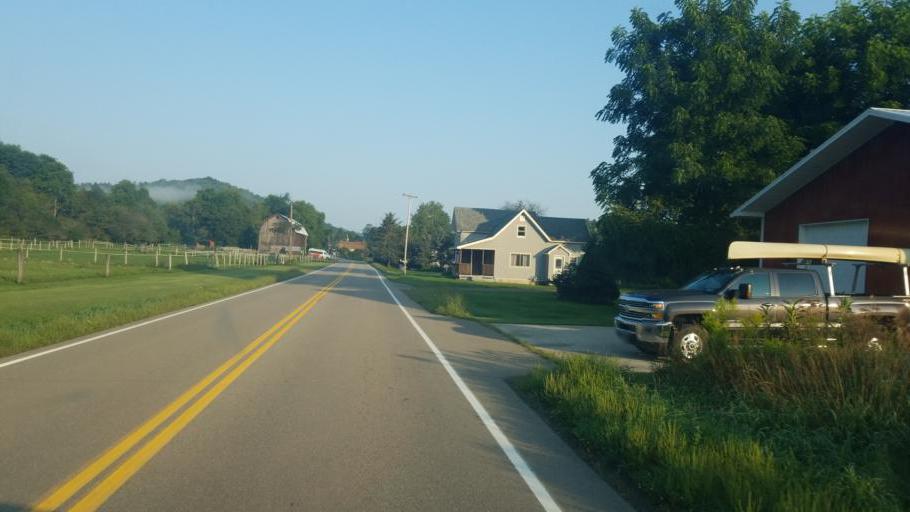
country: US
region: Pennsylvania
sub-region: Tioga County
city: Westfield
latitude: 41.9913
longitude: -77.4906
